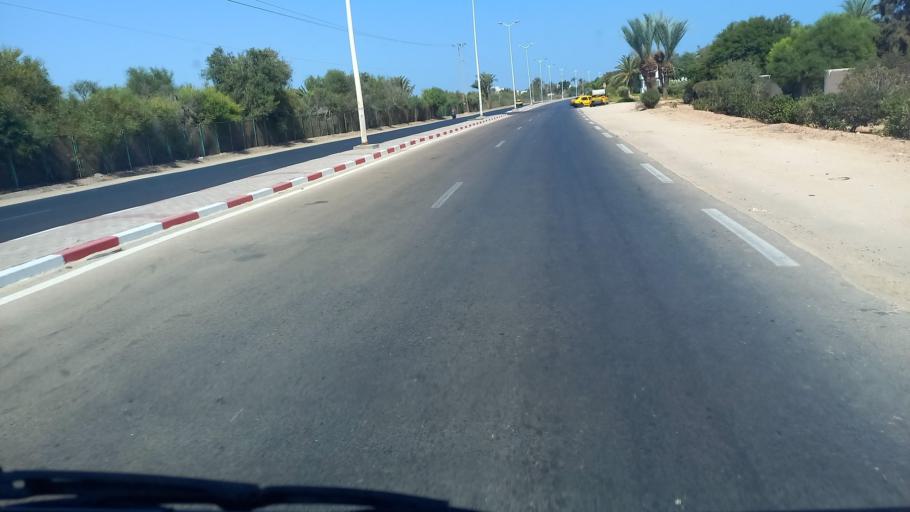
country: TN
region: Madanin
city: Midoun
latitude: 33.8297
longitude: 11.0081
